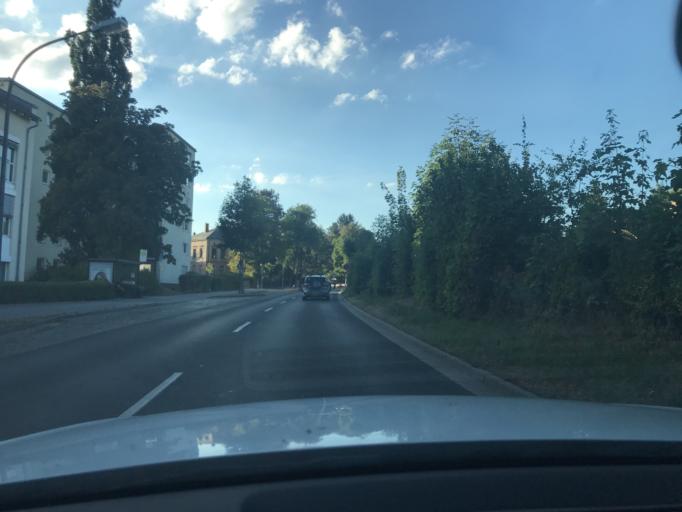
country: DE
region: Bavaria
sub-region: Upper Franconia
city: Bayreuth
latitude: 49.9385
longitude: 11.5880
